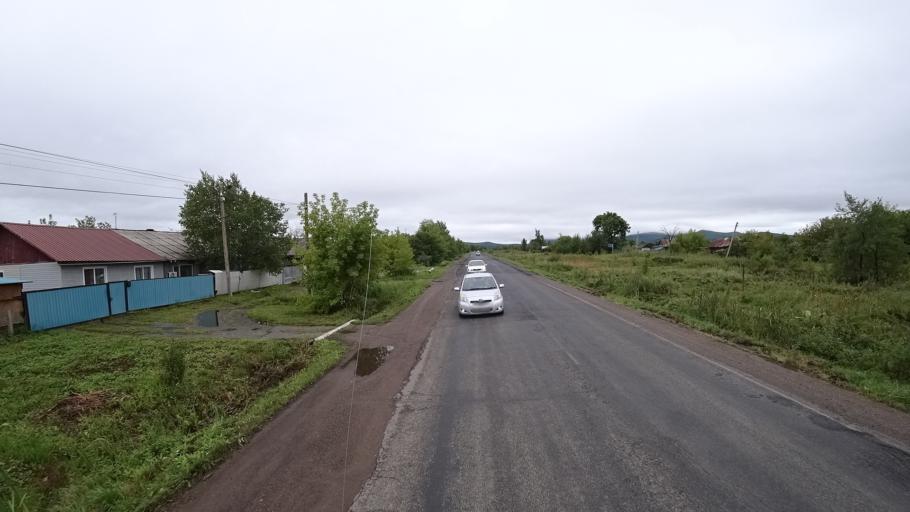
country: RU
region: Primorskiy
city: Monastyrishche
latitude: 44.1995
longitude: 132.4771
